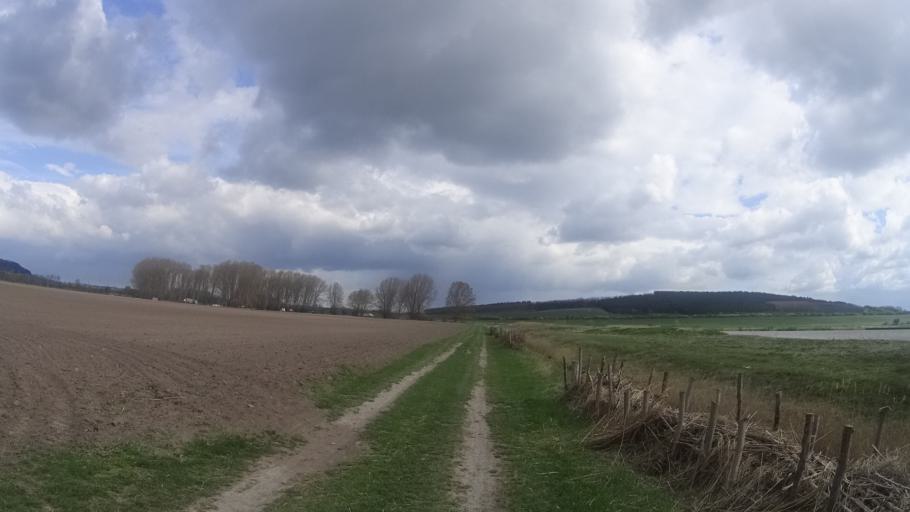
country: DE
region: Thuringia
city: Wandersleben
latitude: 50.8671
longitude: 10.8565
